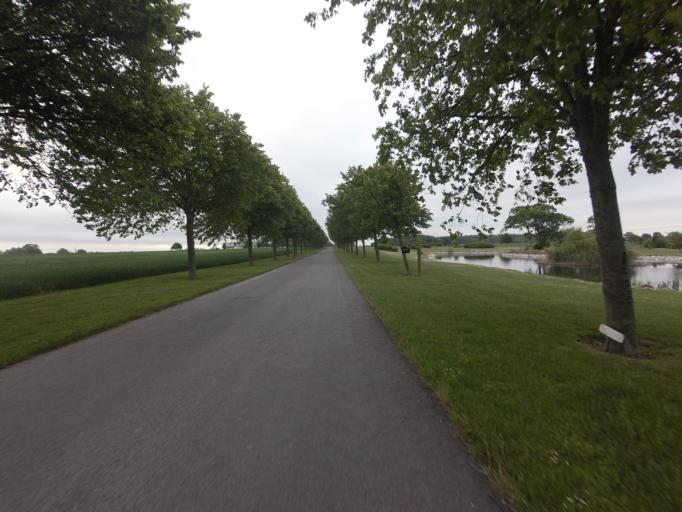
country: SE
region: Skane
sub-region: Angelholms Kommun
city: Strovelstorp
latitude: 56.1356
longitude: 12.7868
